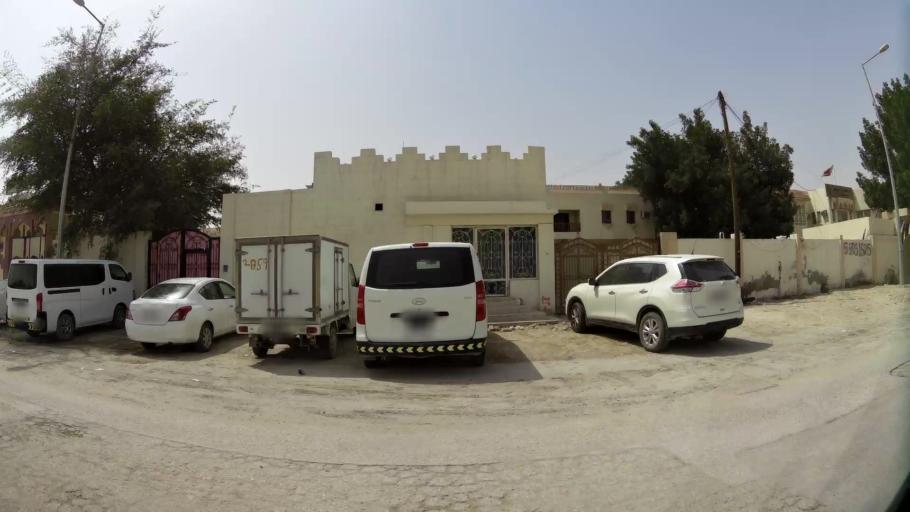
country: QA
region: Baladiyat ar Rayyan
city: Ar Rayyan
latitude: 25.2371
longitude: 51.4307
